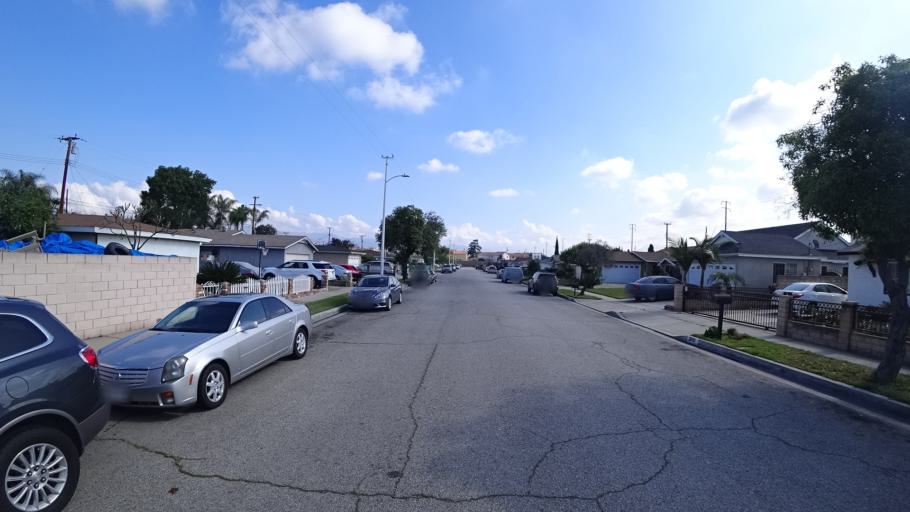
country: US
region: California
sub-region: Los Angeles County
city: Baldwin Park
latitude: 34.0726
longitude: -117.9666
